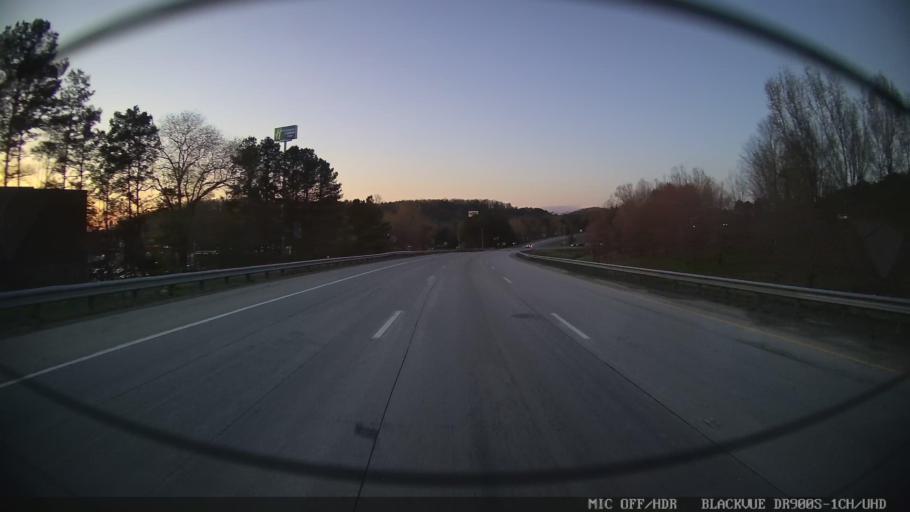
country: US
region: Georgia
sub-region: Bartow County
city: Cartersville
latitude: 34.2057
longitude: -84.7523
